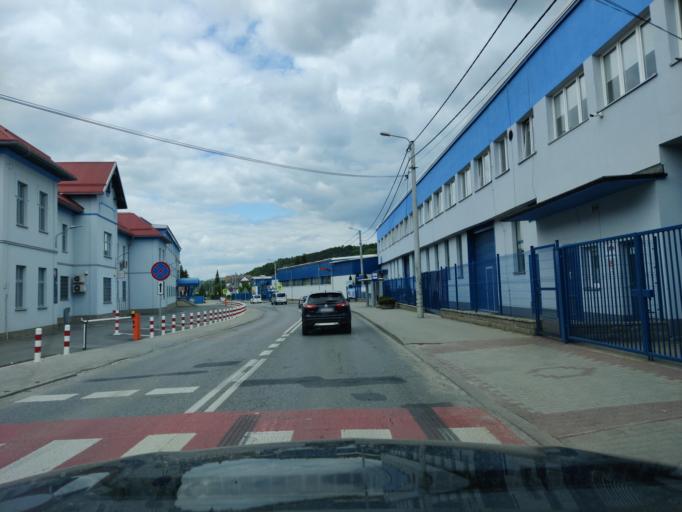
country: PL
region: Lesser Poland Voivodeship
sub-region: Powiat myslenicki
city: Sulkowice
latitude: 49.8505
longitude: 19.8012
